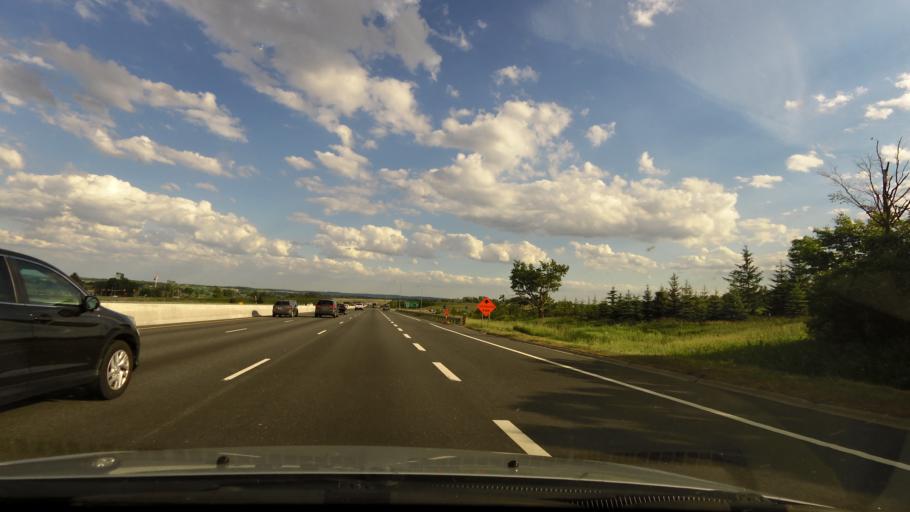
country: CA
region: Ontario
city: Bradford West Gwillimbury
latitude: 44.1034
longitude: -79.6319
